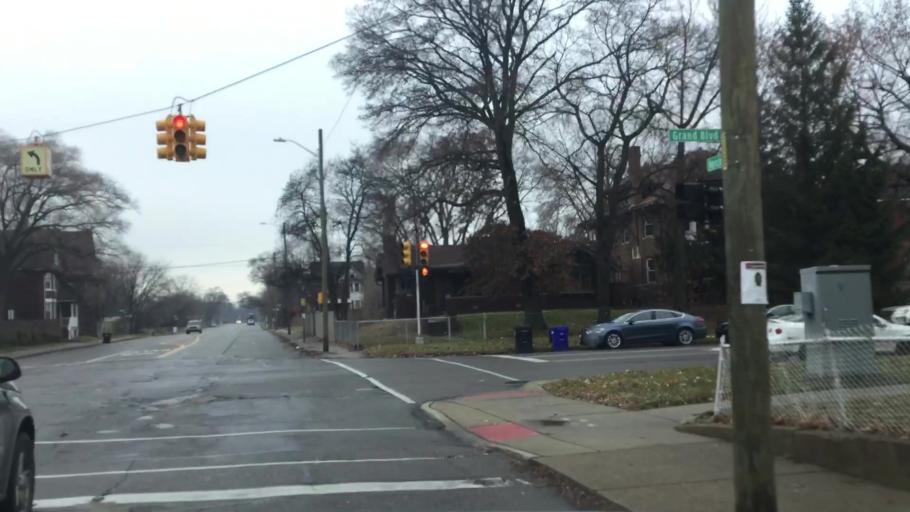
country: US
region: Michigan
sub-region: Wayne County
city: Detroit
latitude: 42.3558
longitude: -83.0072
